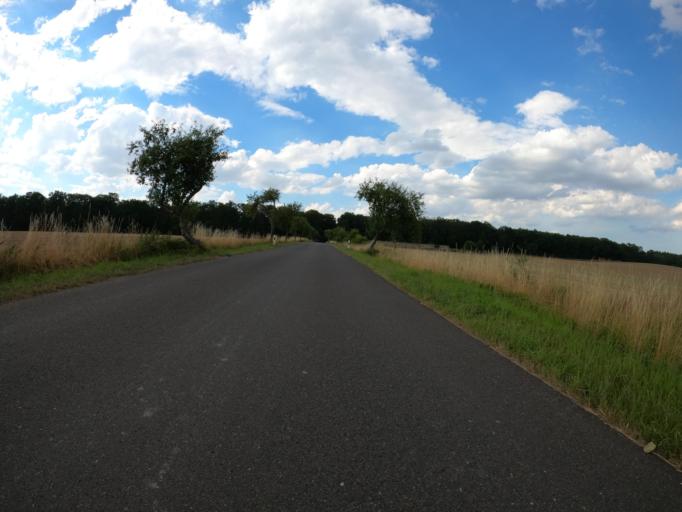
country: DE
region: Mecklenburg-Vorpommern
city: Woldegk
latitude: 53.4274
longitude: 13.6025
